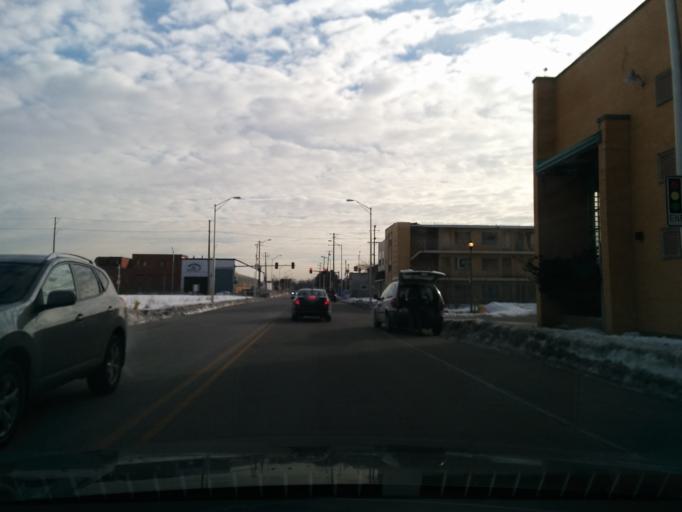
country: US
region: Illinois
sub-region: Cook County
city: Maywood
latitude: 41.8881
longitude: -87.8459
